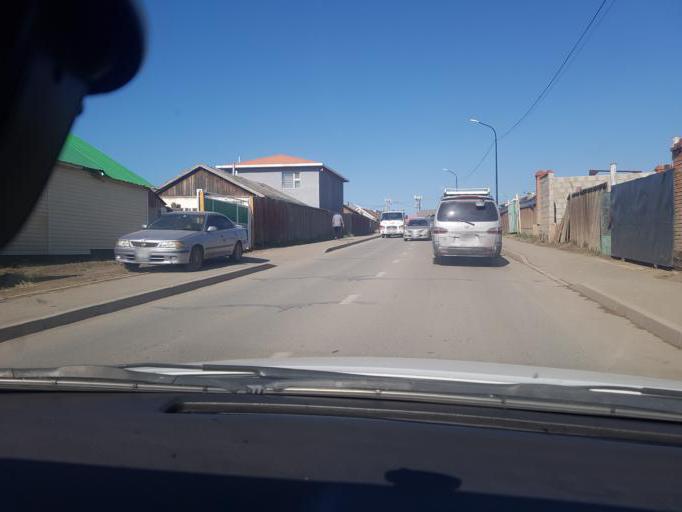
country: MN
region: Ulaanbaatar
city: Ulaanbaatar
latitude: 47.9493
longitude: 106.8662
